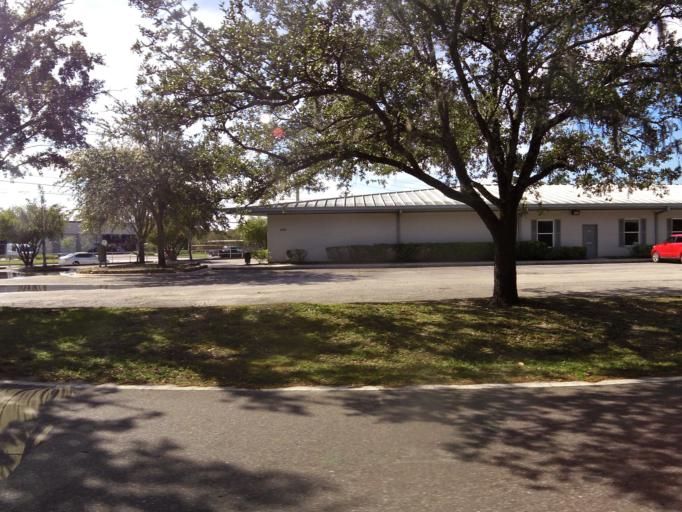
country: US
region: Florida
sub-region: Duval County
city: Jacksonville
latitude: 30.2654
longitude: -81.6128
